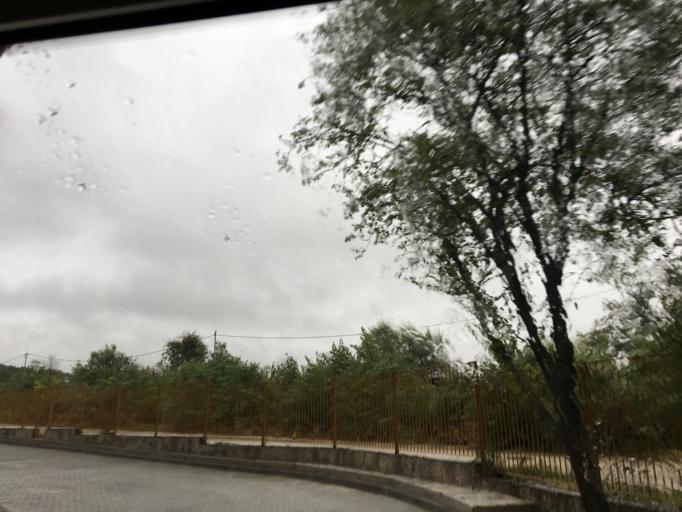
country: BG
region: Lovech
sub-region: Obshtina Lovech
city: Lovech
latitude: 43.1608
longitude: 24.7138
